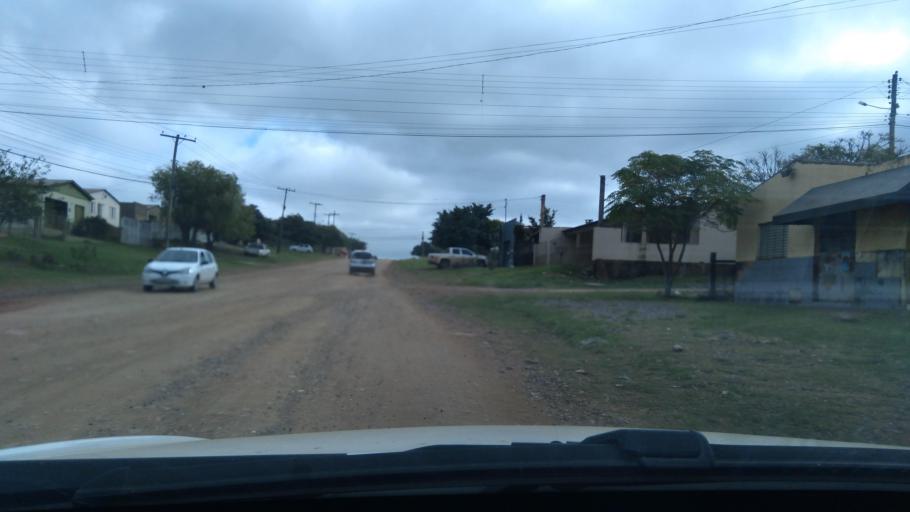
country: BR
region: Rio Grande do Sul
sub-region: Dom Pedrito
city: Dom Pedrito
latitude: -30.9813
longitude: -54.6552
